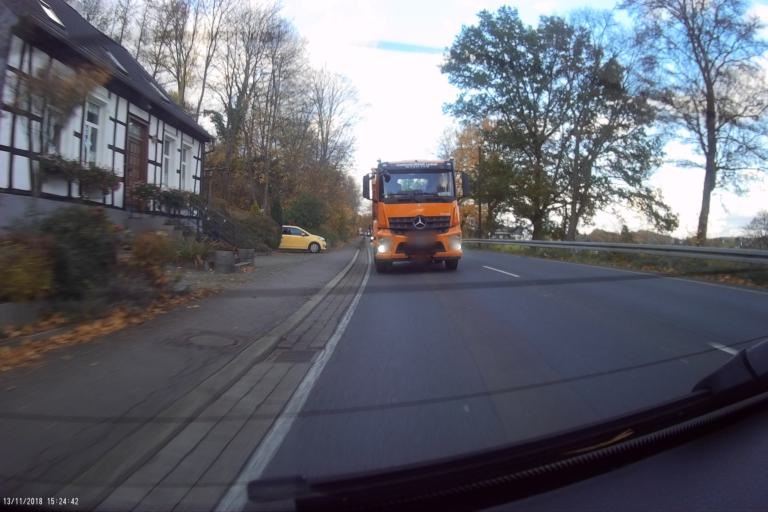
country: DE
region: North Rhine-Westphalia
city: Hattingen
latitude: 51.3900
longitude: 7.1926
